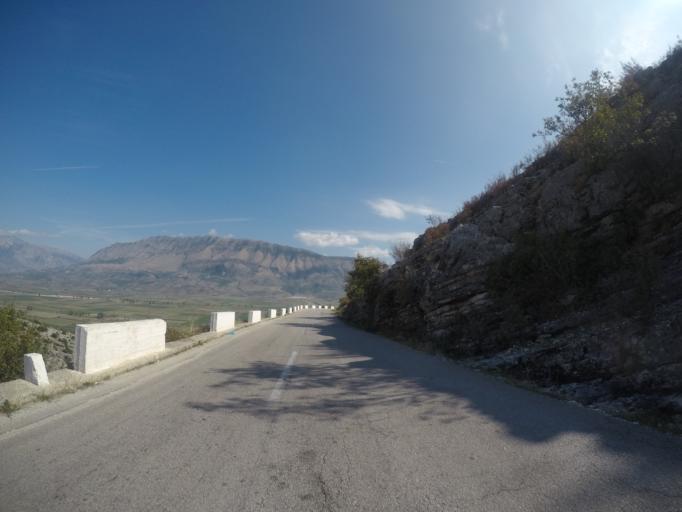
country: AL
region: Gjirokaster
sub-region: Rrethi i Gjirokastres
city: Libohove
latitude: 39.9479
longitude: 20.2432
